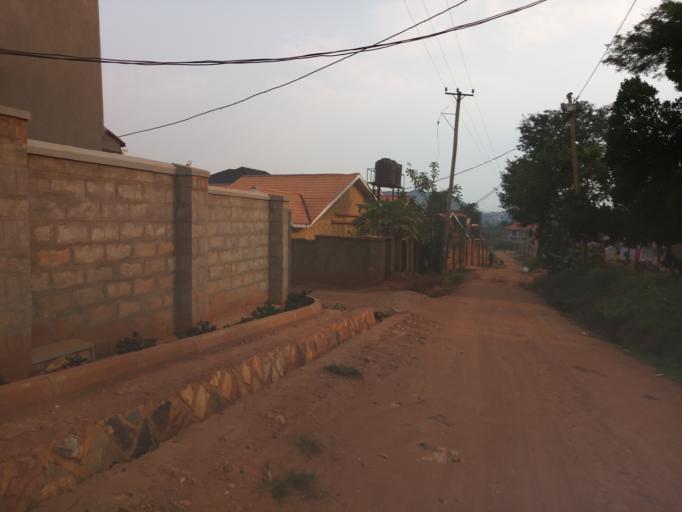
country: UG
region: Central Region
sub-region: Wakiso District
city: Kireka
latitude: 0.3905
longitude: 32.6390
